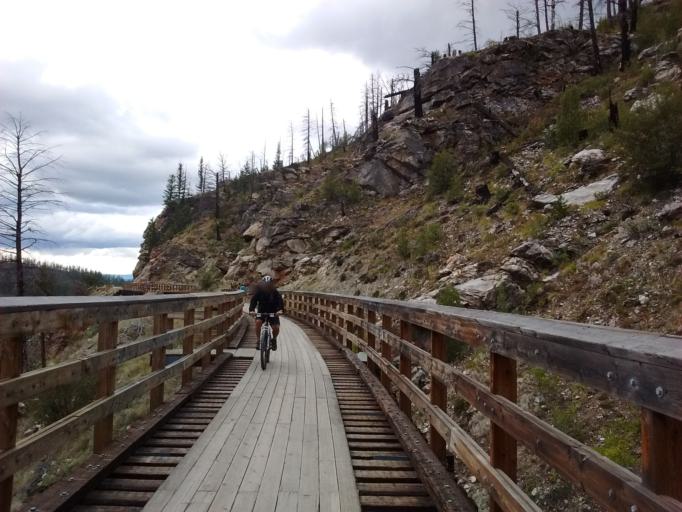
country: CA
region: British Columbia
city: Kelowna
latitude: 49.7879
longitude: -119.3085
